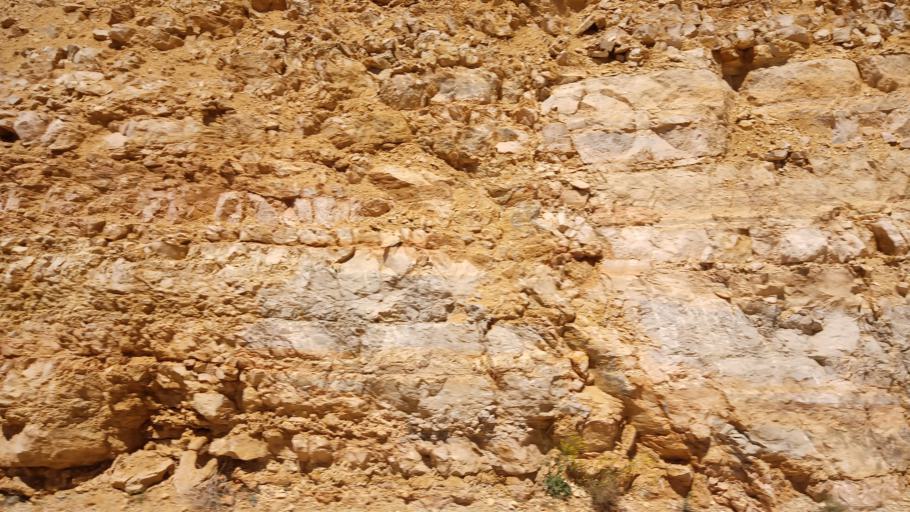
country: TR
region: Malatya
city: Darende
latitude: 38.6260
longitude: 37.4559
